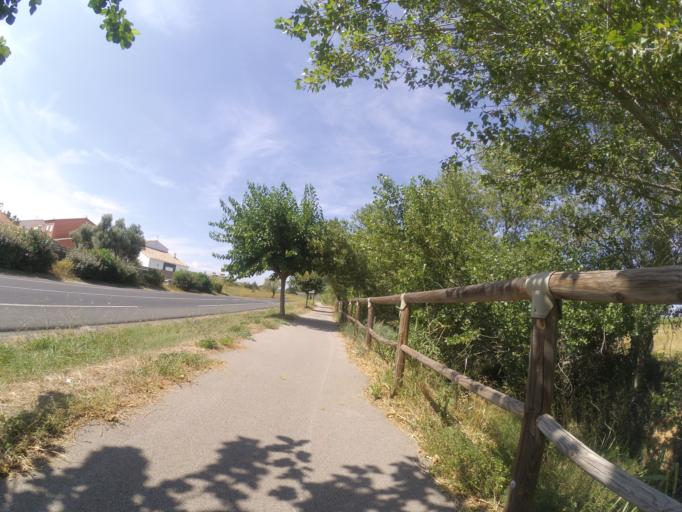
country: FR
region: Languedoc-Roussillon
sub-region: Departement des Pyrenees-Orientales
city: Peyrestortes
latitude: 42.7558
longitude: 2.8416
